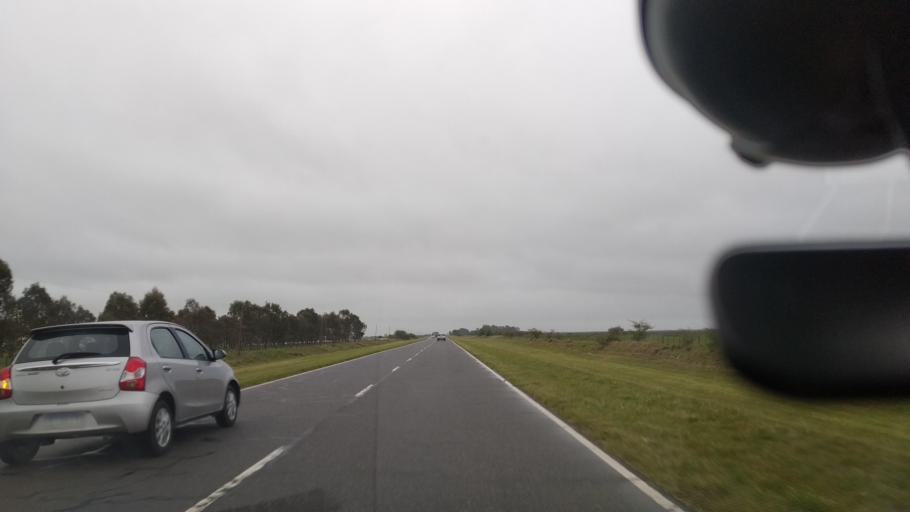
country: AR
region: Buenos Aires
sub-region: Partido de Dolores
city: Dolores
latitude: -36.0692
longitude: -57.4402
